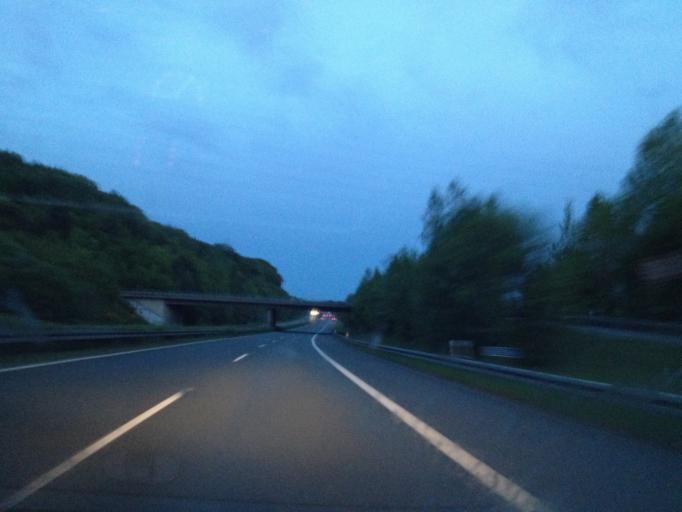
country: DE
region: North Rhine-Westphalia
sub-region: Regierungsbezirk Arnsberg
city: Arnsberg
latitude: 51.4391
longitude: 7.9905
